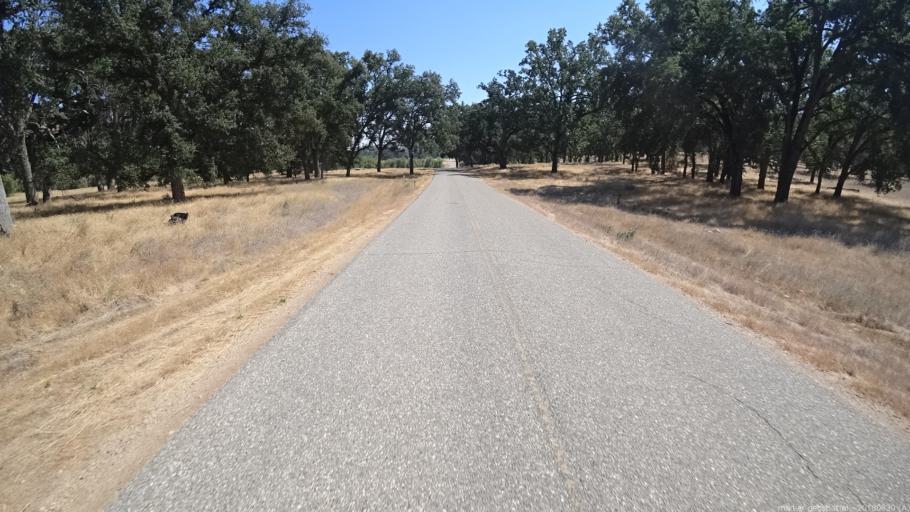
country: US
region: California
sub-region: Monterey County
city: King City
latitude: 36.0495
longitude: -121.3024
